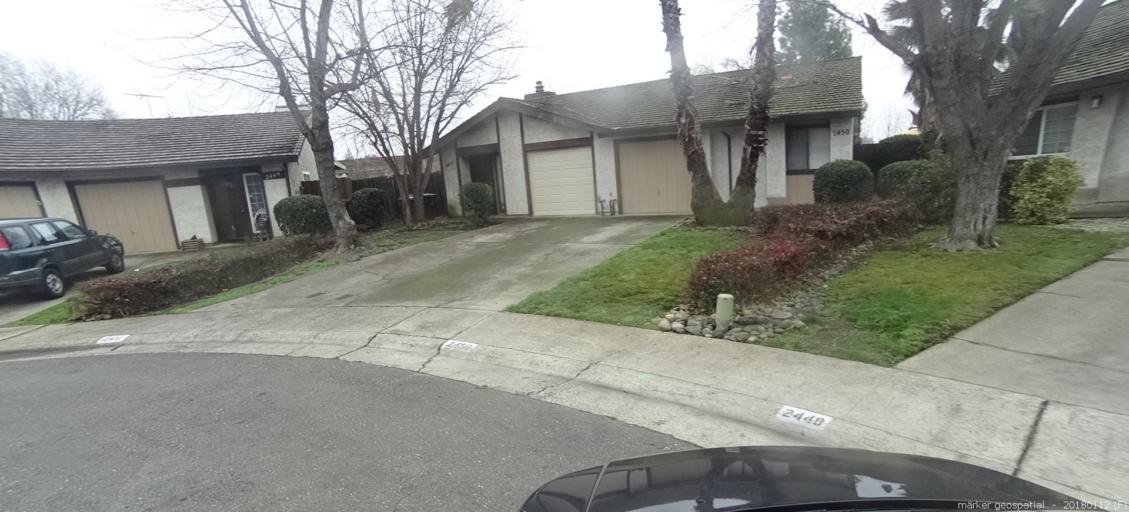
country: US
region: California
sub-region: Sacramento County
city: Gold River
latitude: 38.6101
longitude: -121.2730
